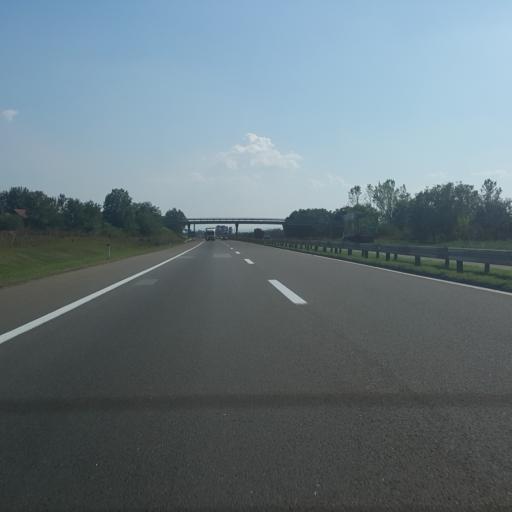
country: RS
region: Central Serbia
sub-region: Podunavski Okrug
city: Velika Plana
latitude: 44.3099
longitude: 21.0935
